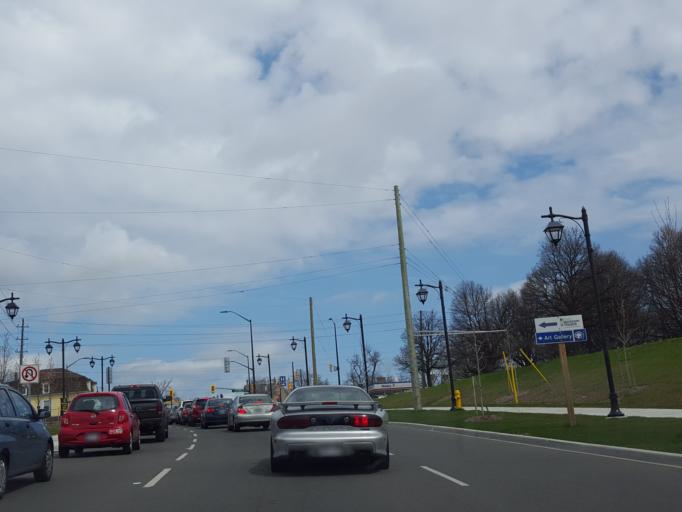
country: CA
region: Ontario
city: Markham
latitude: 43.8728
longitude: -79.2593
